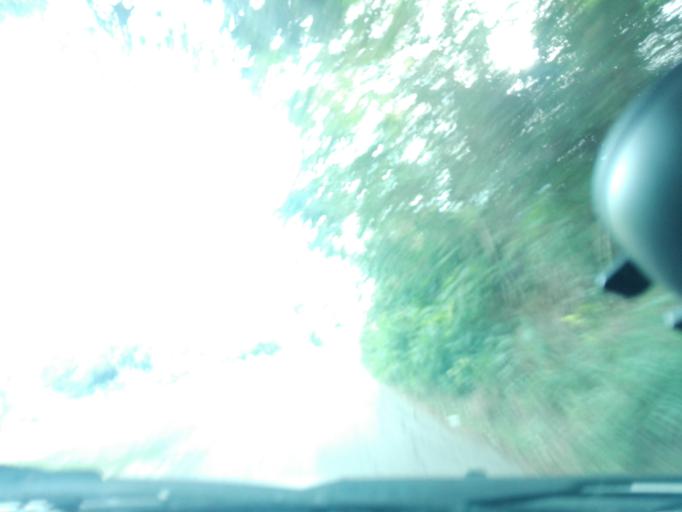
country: IT
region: Abruzzo
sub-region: Provincia di Pescara
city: Cappelle sul Tavo
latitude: 42.4581
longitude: 14.1035
